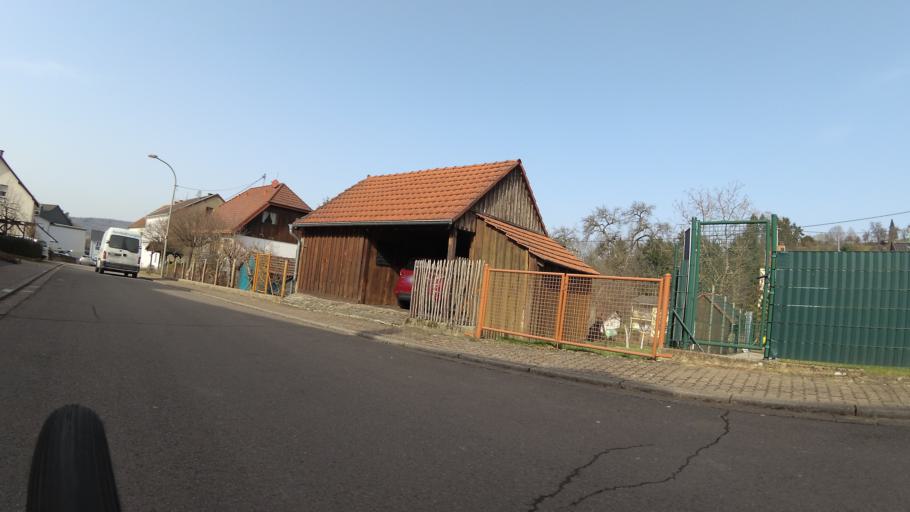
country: DE
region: Saarland
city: Nalbach
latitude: 49.4132
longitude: 6.7697
